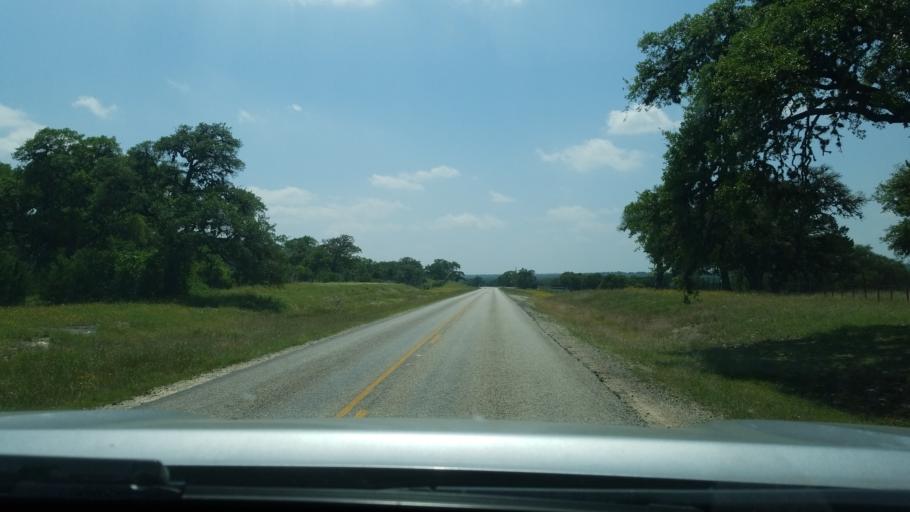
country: US
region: Texas
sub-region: Blanco County
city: Blanco
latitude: 29.9674
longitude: -98.5274
